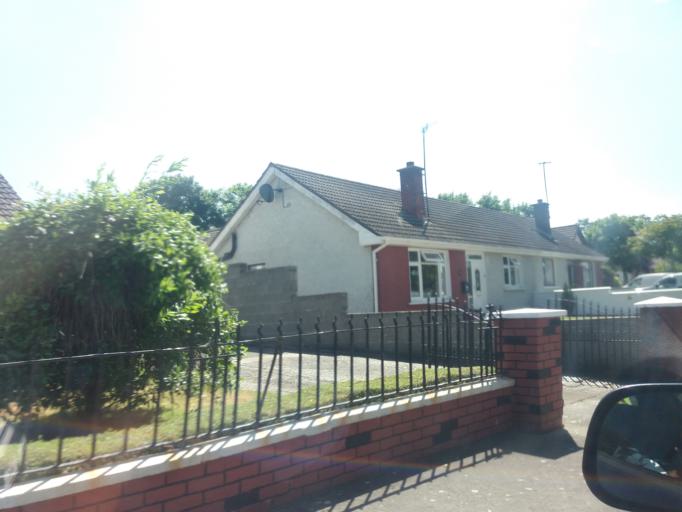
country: IE
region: Leinster
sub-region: An Mhi
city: Stamullin
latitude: 53.5824
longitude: -6.2859
